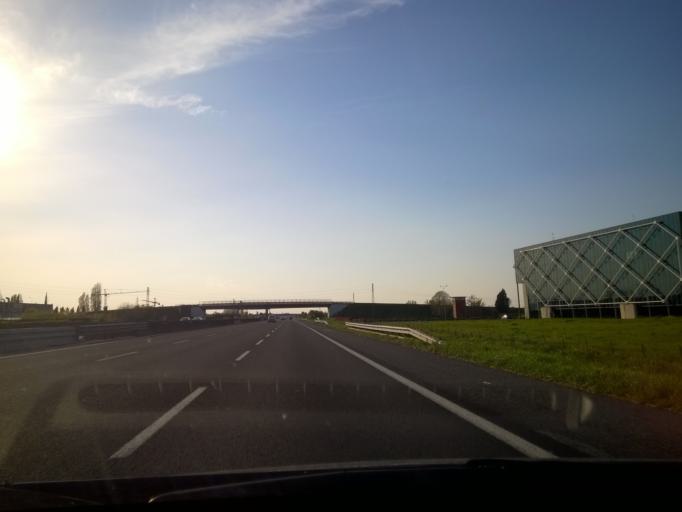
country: IT
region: Emilia-Romagna
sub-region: Provincia di Bologna
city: Imola
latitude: 44.3844
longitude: 11.7319
